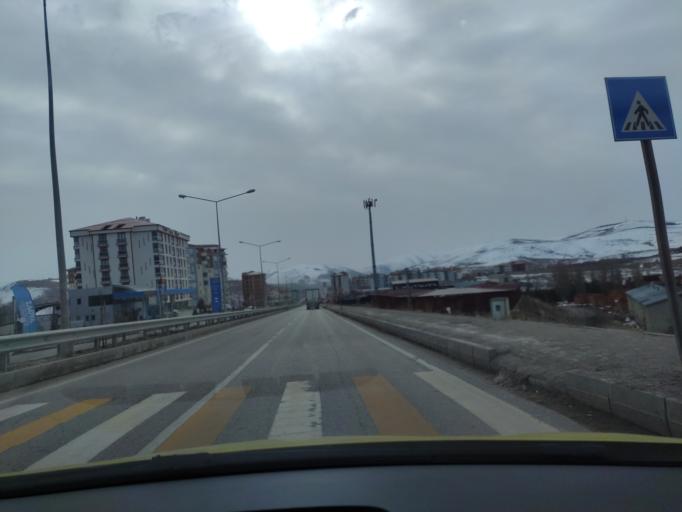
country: TR
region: Bayburt
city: Bayburt
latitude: 40.2709
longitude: 40.1950
